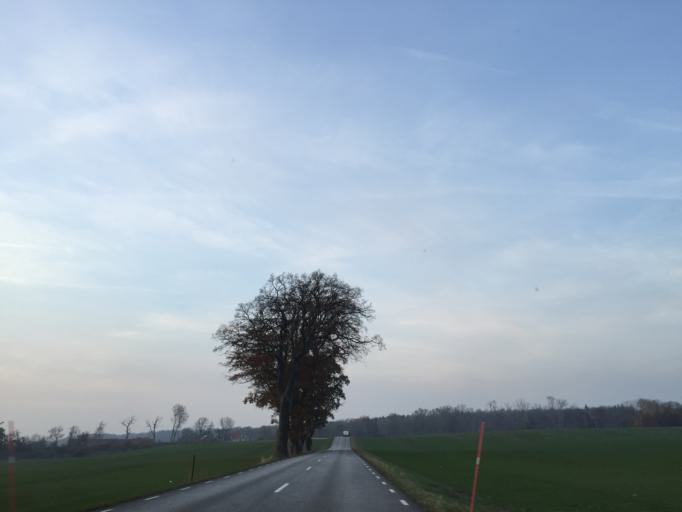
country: SE
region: Skane
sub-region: Sjobo Kommun
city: Blentarp
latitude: 55.6958
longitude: 13.6030
